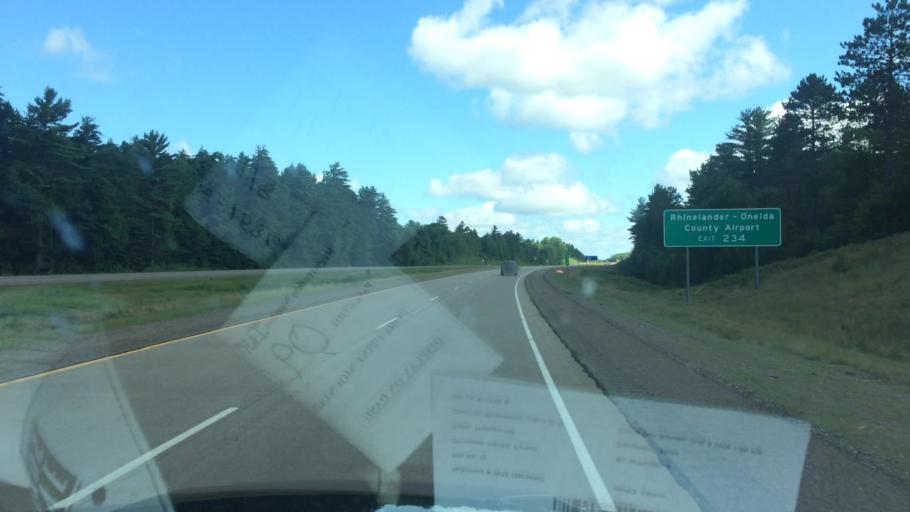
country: US
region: Wisconsin
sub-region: Lincoln County
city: Tomahawk
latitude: 45.5279
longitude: -89.6752
